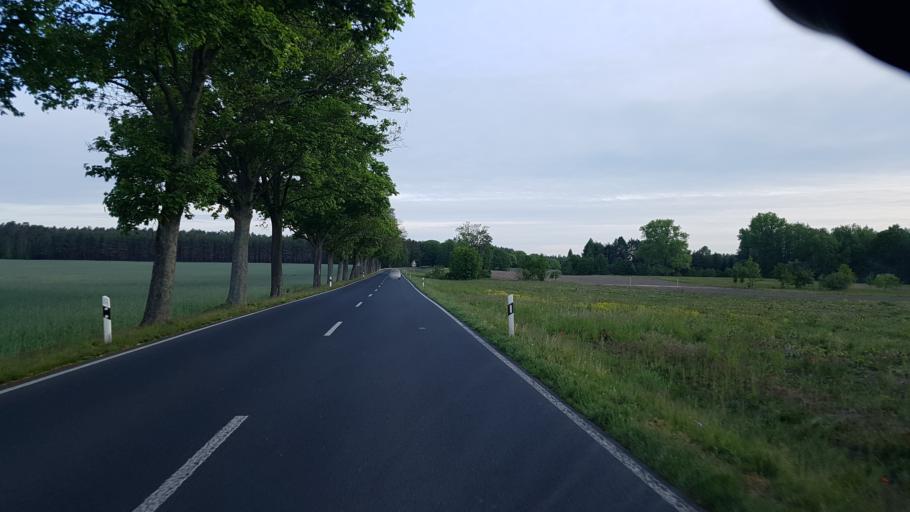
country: DE
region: Brandenburg
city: Sonnewalde
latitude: 51.7464
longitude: 13.6797
